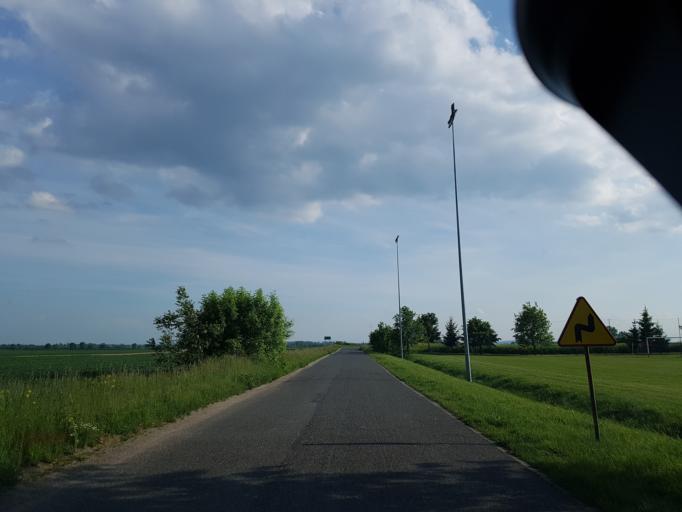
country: PL
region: Lower Silesian Voivodeship
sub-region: Powiat strzelinski
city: Wiazow
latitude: 50.8416
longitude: 17.2098
